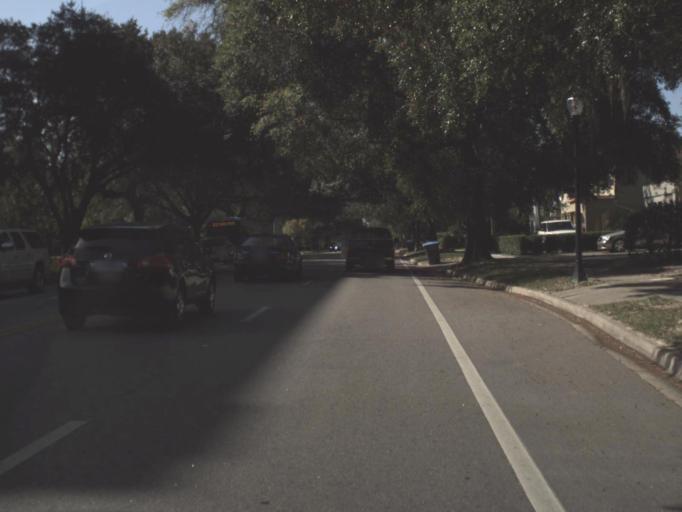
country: US
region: Florida
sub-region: Orange County
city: Fairview Shores
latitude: 28.5853
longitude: -81.3658
